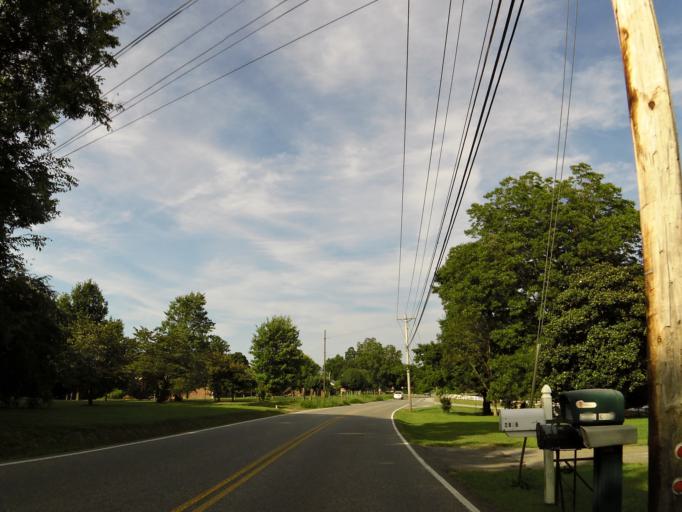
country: US
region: Tennessee
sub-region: Blount County
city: Eagleton Village
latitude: 35.7704
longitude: -83.9164
